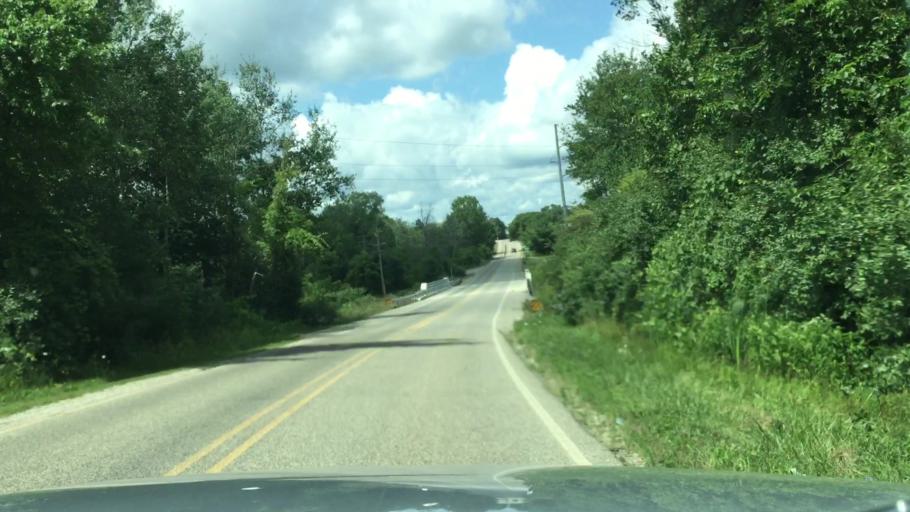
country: US
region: Michigan
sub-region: Ionia County
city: Belding
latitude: 43.1094
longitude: -85.2104
